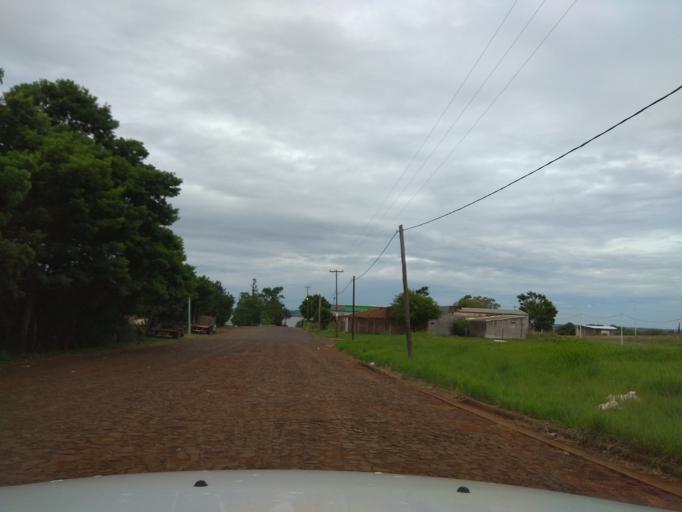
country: AR
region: Misiones
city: Garupa
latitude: -27.4515
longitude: -55.8584
